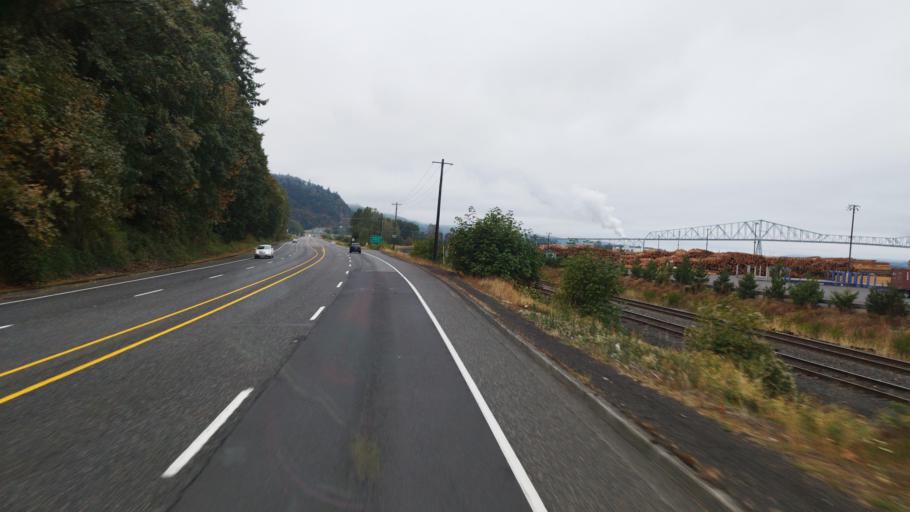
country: US
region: Oregon
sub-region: Columbia County
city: Rainier
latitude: 46.0936
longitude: -122.9493
